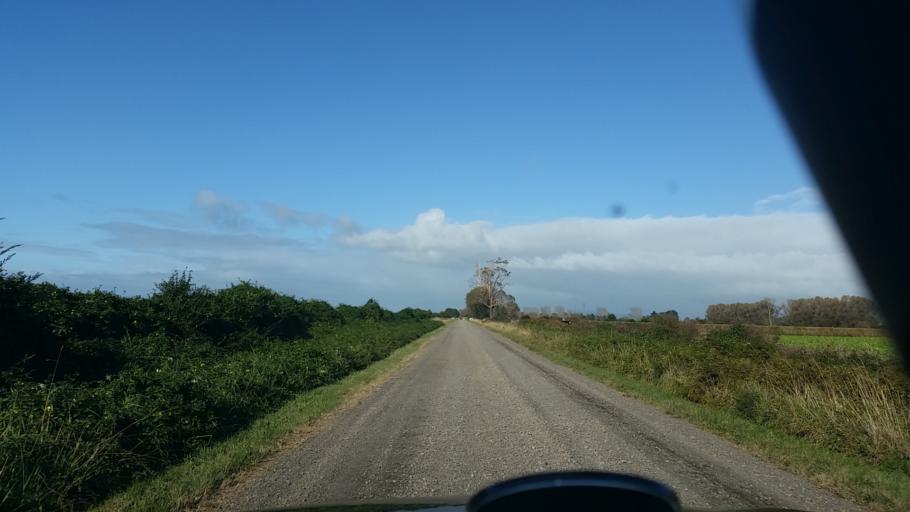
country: NZ
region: Bay of Plenty
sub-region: Western Bay of Plenty District
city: Katikati
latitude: -37.5849
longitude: 175.7131
